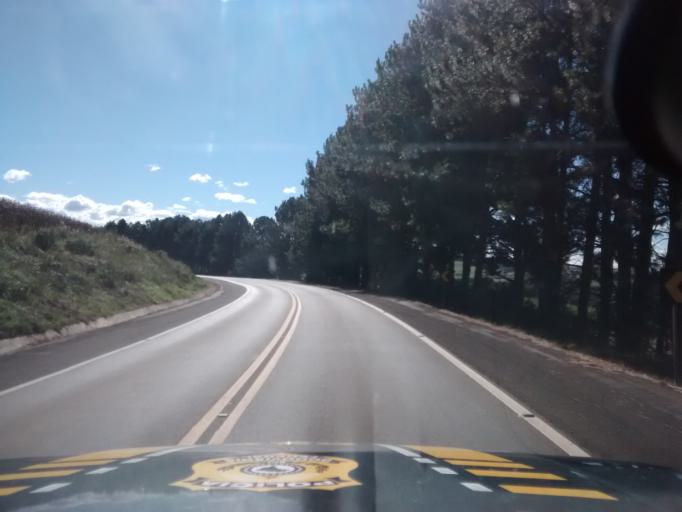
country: BR
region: Rio Grande do Sul
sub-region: Vacaria
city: Vacaria
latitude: -28.3465
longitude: -51.1439
